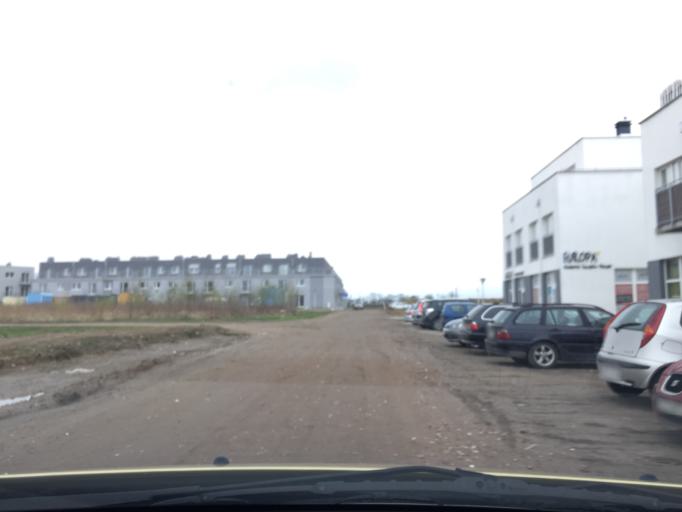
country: PL
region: Greater Poland Voivodeship
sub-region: Powiat poznanski
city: Plewiska
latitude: 52.3754
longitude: 16.8094
